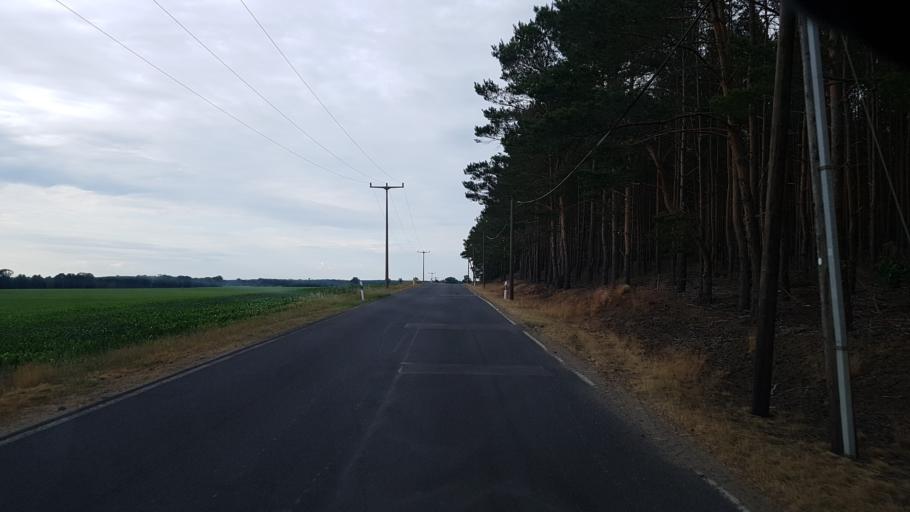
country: DE
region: Brandenburg
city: Golssen
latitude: 51.9444
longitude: 13.6255
